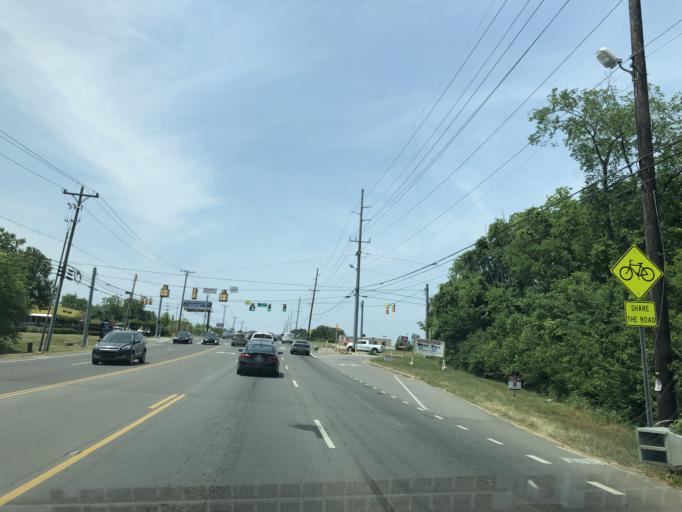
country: US
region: Tennessee
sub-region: Rutherford County
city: La Vergne
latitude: 36.0498
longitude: -86.6142
